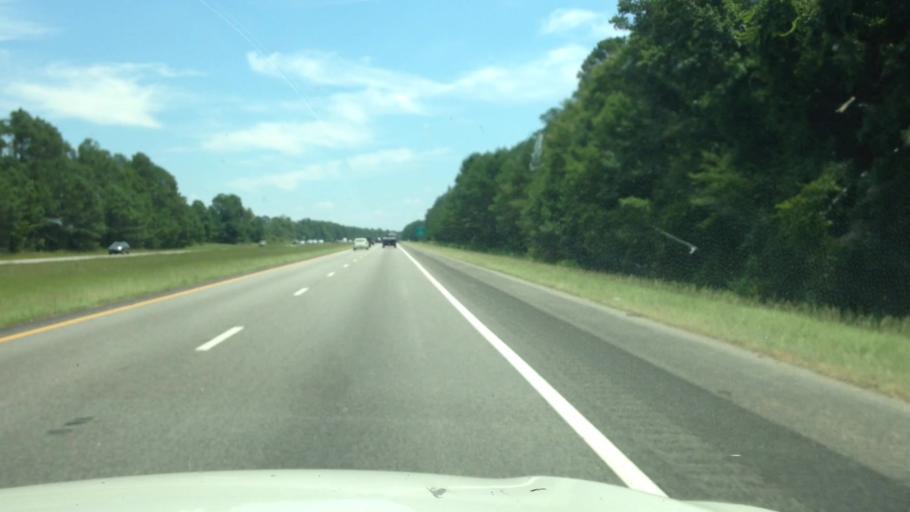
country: US
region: South Carolina
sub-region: Florence County
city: Timmonsville
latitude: 34.2032
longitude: -79.8906
